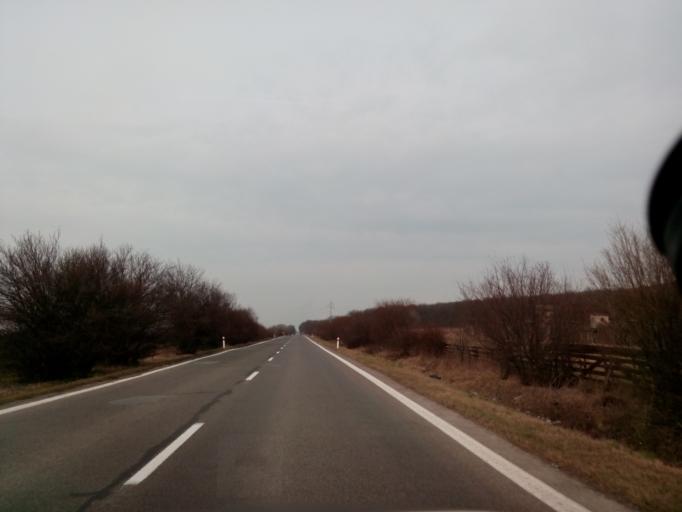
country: HU
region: Borsod-Abauj-Zemplen
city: Satoraljaujhely
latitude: 48.4958
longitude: 21.6504
